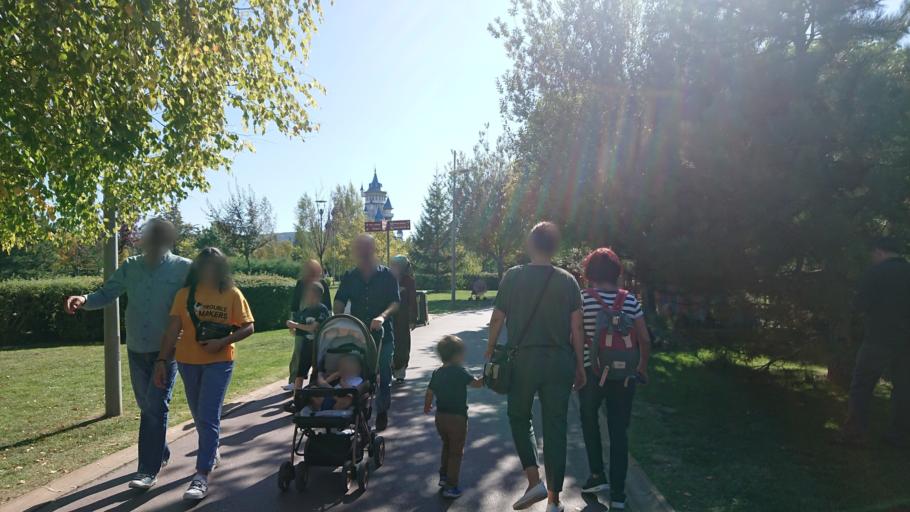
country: TR
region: Eskisehir
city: Eskisehir
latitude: 39.7628
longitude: 30.4739
